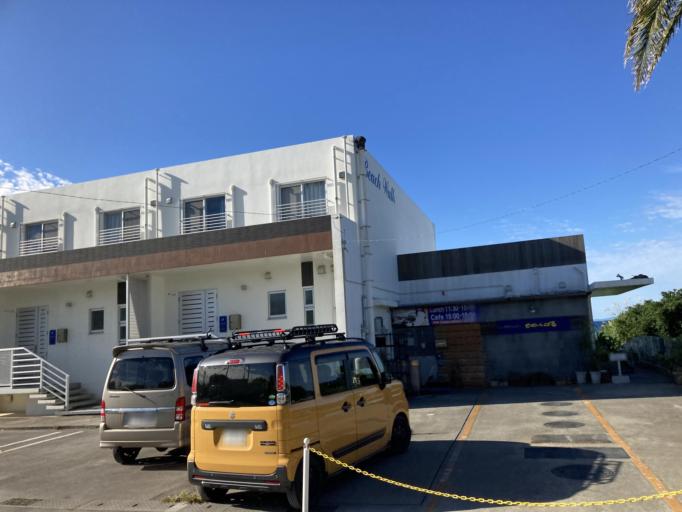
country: JP
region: Okinawa
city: Chatan
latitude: 26.3700
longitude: 127.7353
